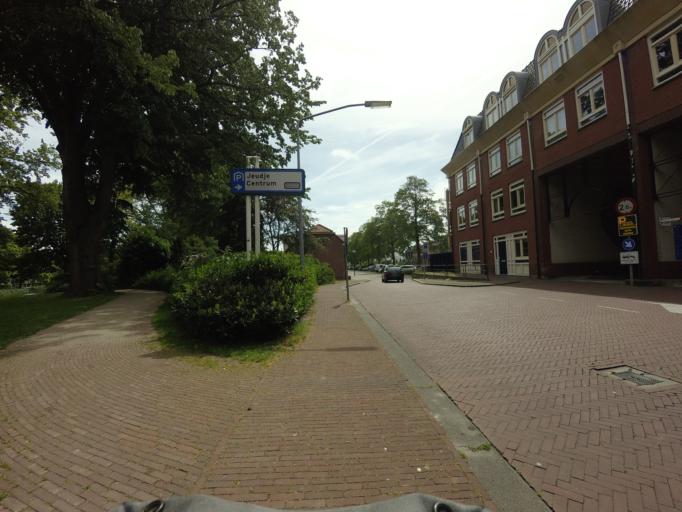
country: NL
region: North Holland
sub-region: Gemeente Hoorn
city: Hoorn
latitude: 52.6428
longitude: 5.0634
